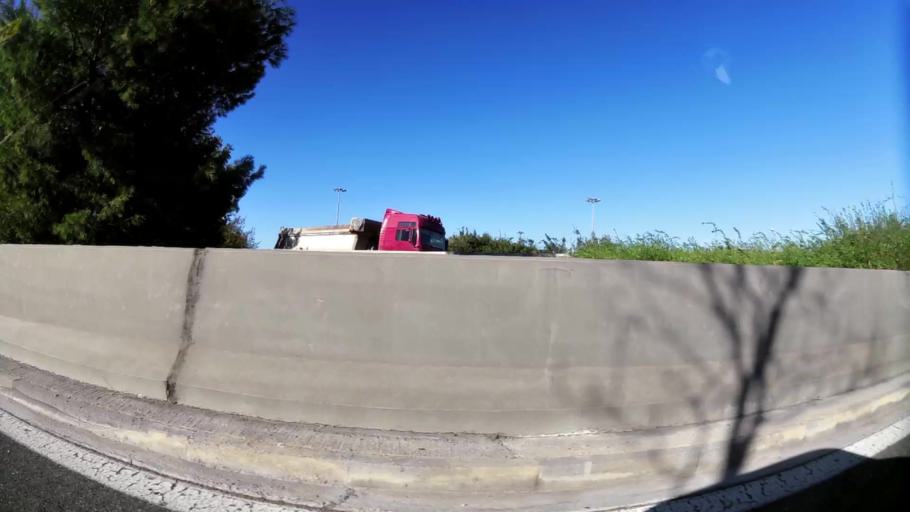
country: GR
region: Attica
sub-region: Nomarchia Athinas
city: Metamorfosi
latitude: 38.0629
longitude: 23.7508
